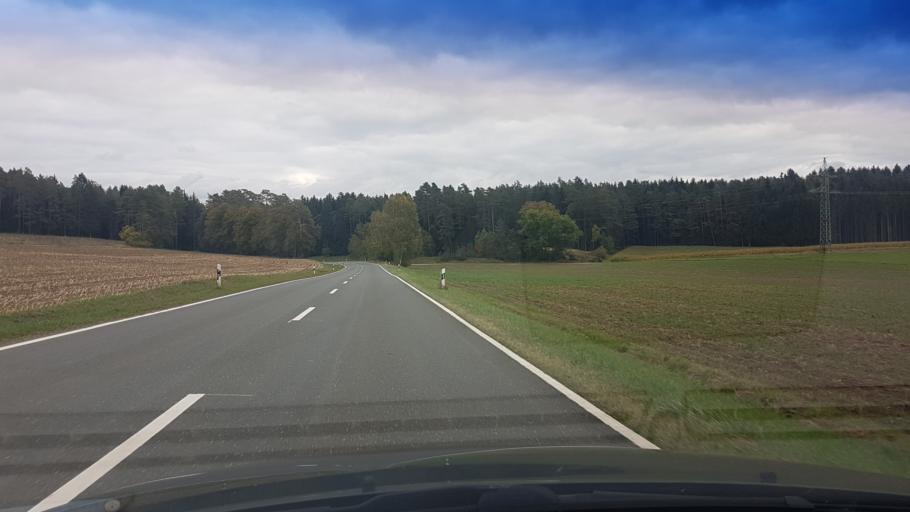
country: DE
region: Bavaria
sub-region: Upper Franconia
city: Stadelhofen
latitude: 50.0102
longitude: 11.2154
